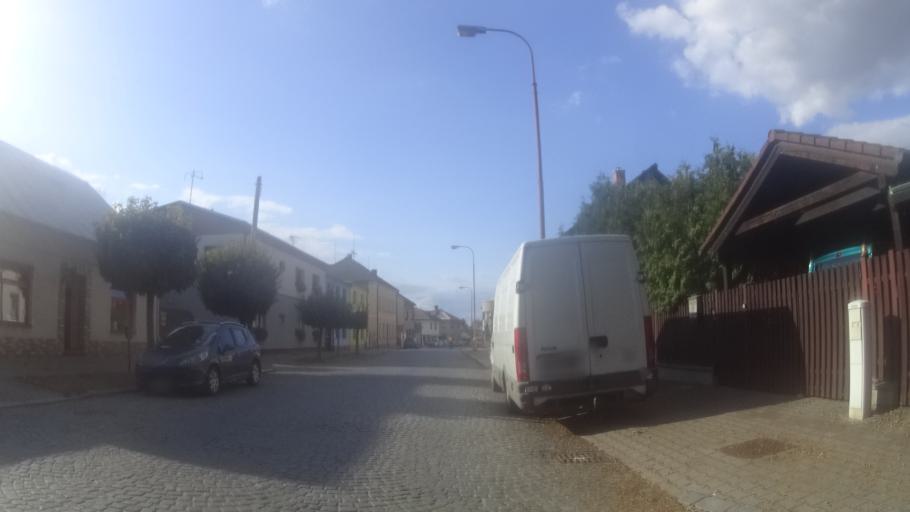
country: CZ
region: Kralovehradecky
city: Trebechovice pod Orebem
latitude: 50.1967
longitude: 16.0004
